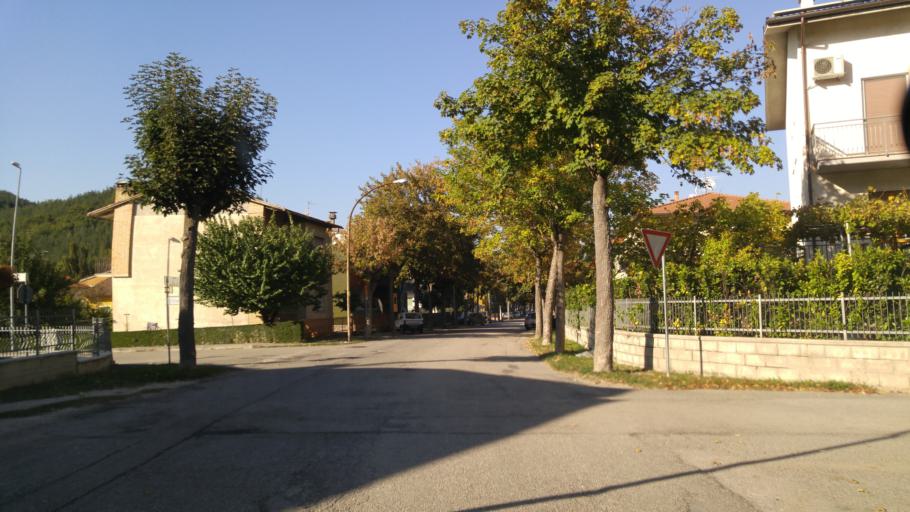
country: IT
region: The Marches
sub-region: Provincia di Pesaro e Urbino
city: Fermignano
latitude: 43.6700
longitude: 12.6439
